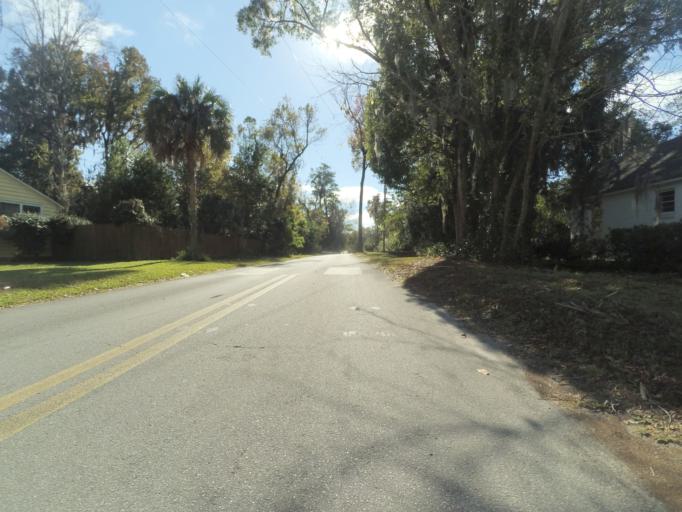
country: US
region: Florida
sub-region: Alachua County
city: Gainesville
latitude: 29.6612
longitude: -82.3372
